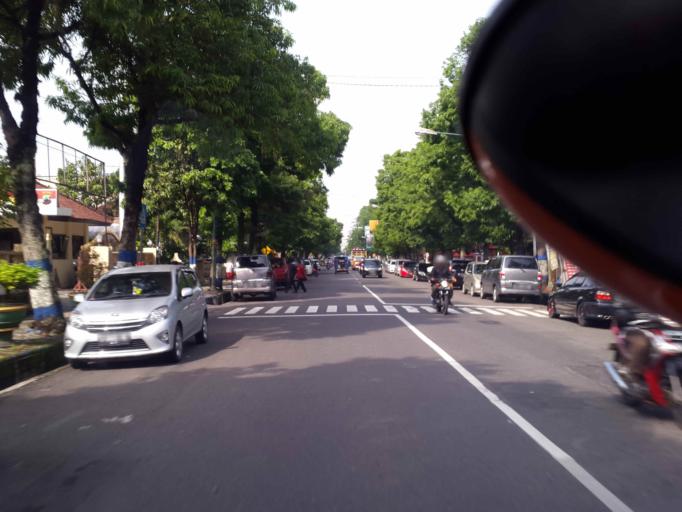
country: ID
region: Central Java
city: Wonosobo
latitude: -7.3965
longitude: 109.7004
